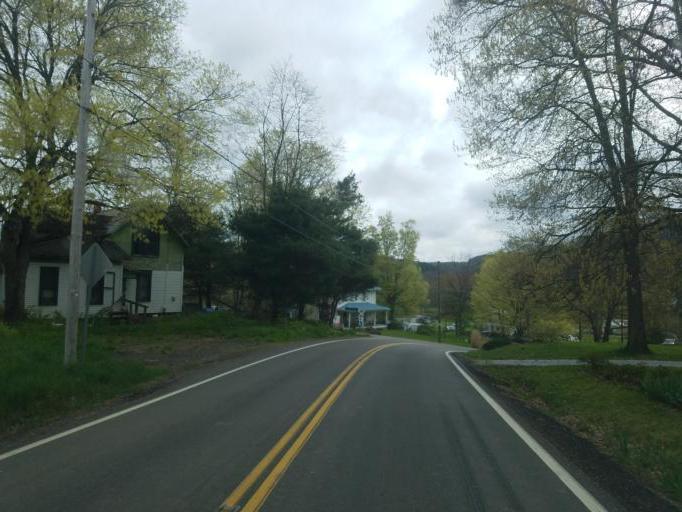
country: US
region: Ohio
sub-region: Knox County
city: Danville
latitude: 40.5220
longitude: -82.2009
